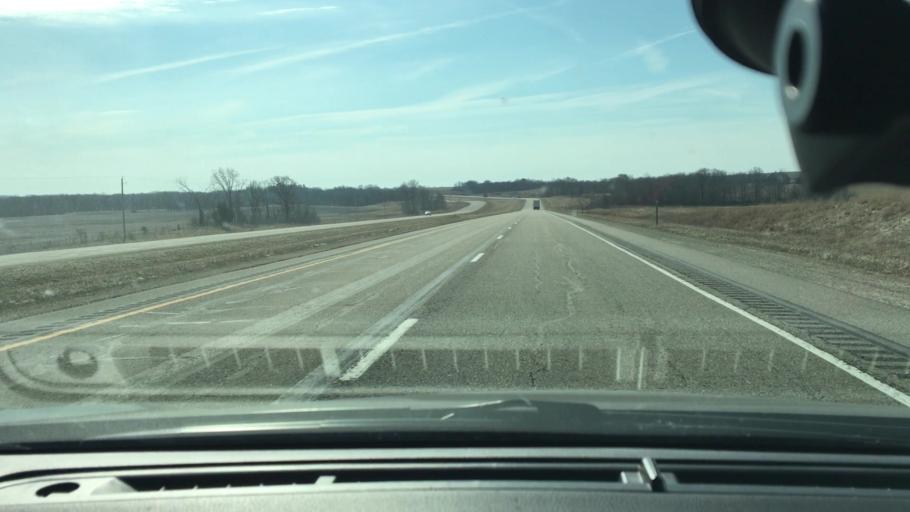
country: US
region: Iowa
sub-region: Chickasaw County
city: Nashua
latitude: 42.9858
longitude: -92.5863
